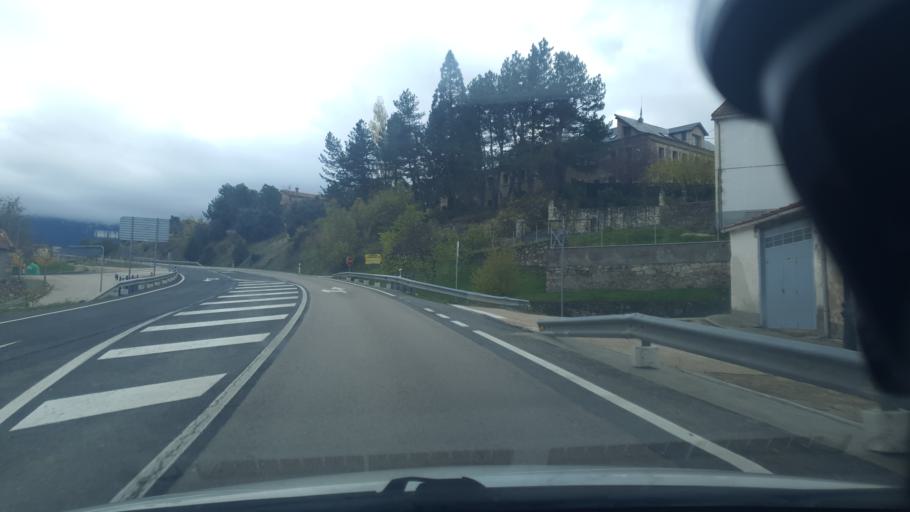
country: ES
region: Castille and Leon
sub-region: Provincia de Segovia
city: Cerezo de Abajo
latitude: 41.2174
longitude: -3.5904
